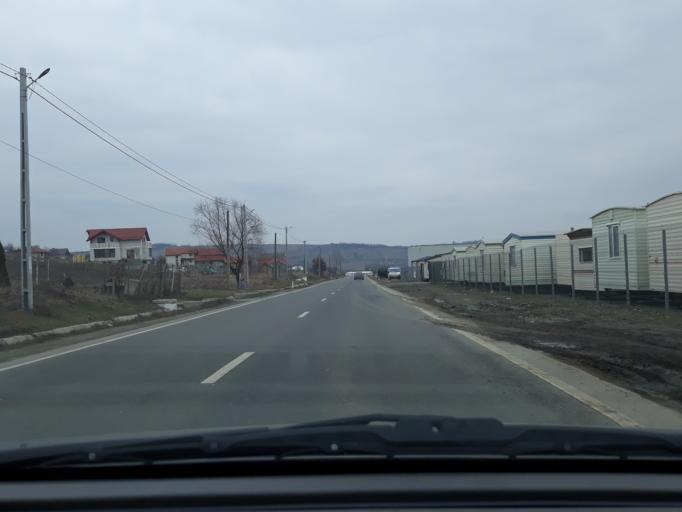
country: RO
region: Salaj
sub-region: Comuna Hereclean
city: Hereclean
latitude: 47.2350
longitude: 22.9819
